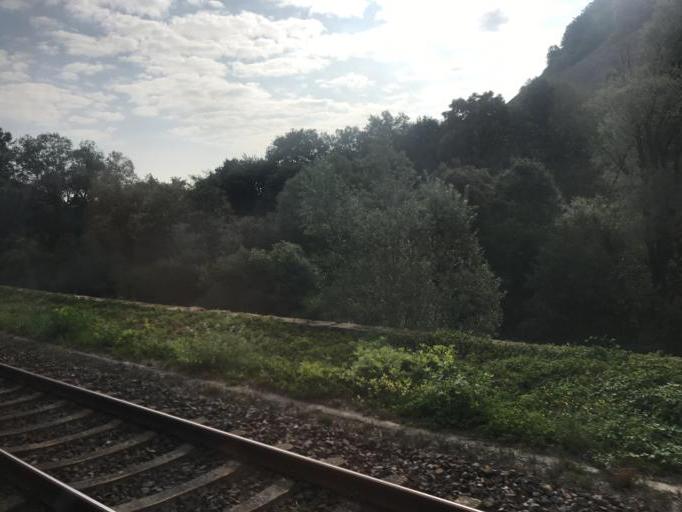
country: DE
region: Rheinland-Pfalz
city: Hochstetten-Dhaun
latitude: 49.7949
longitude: 7.4923
